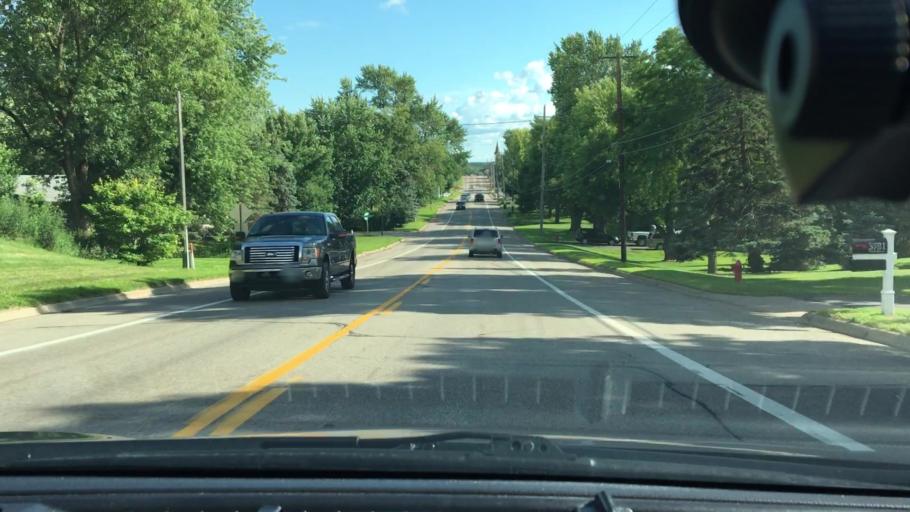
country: US
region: Minnesota
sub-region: Hennepin County
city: Saint Bonifacius
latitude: 44.9099
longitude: -93.7473
